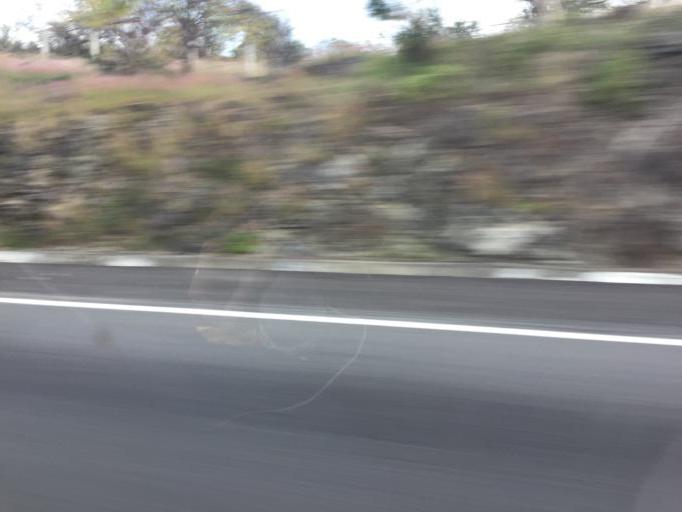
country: MX
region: Michoacan
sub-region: Zinapecuaro
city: Francisco Villa
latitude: 19.8809
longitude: -100.9322
